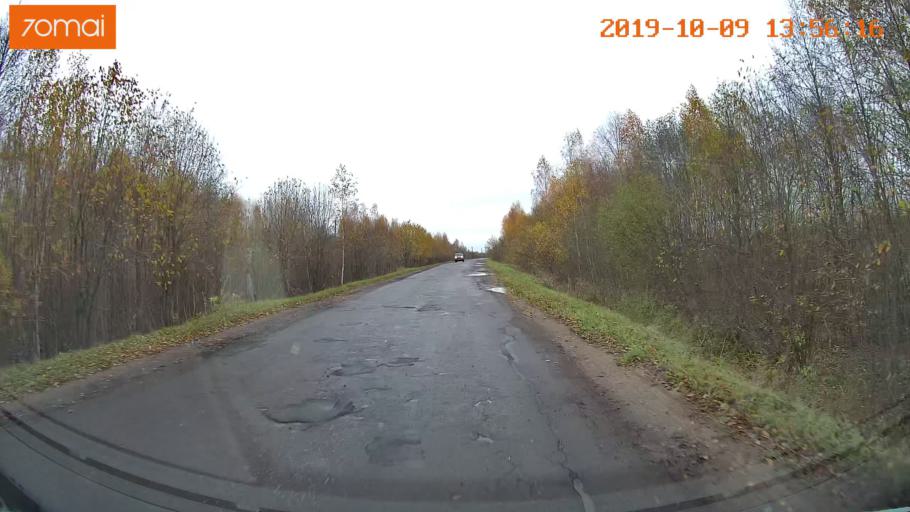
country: RU
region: Kostroma
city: Buy
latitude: 58.4284
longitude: 41.2838
